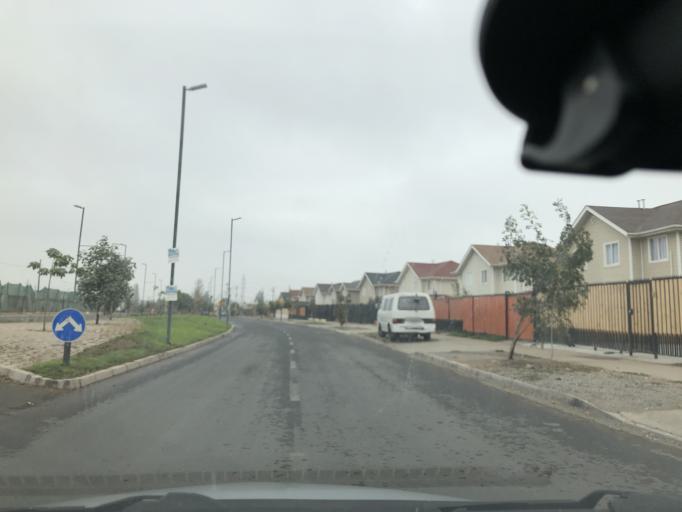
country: CL
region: Santiago Metropolitan
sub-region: Provincia de Cordillera
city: Puente Alto
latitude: -33.5969
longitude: -70.5979
